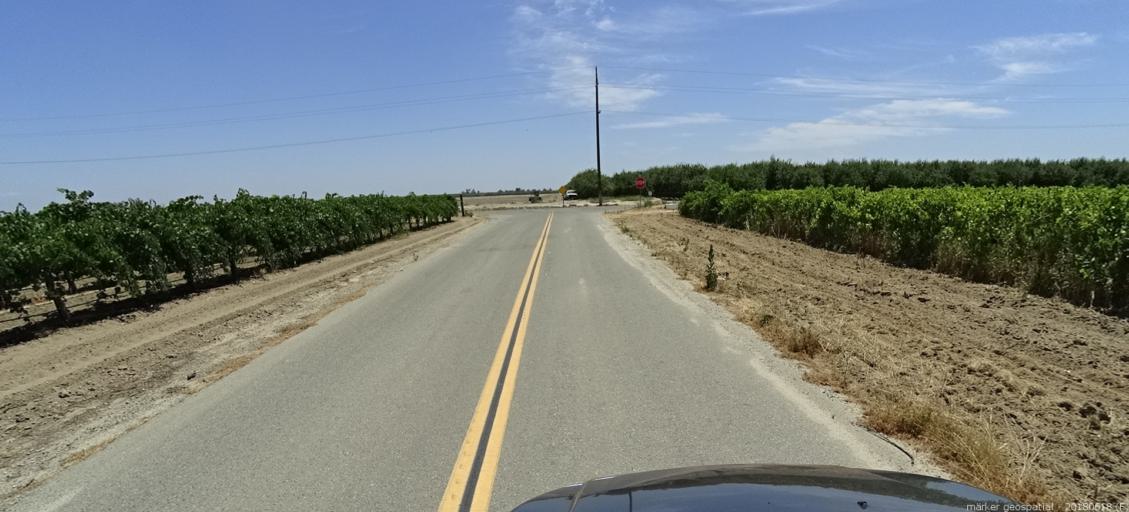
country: US
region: California
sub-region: Madera County
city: Parkwood
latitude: 36.9021
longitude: -120.1112
